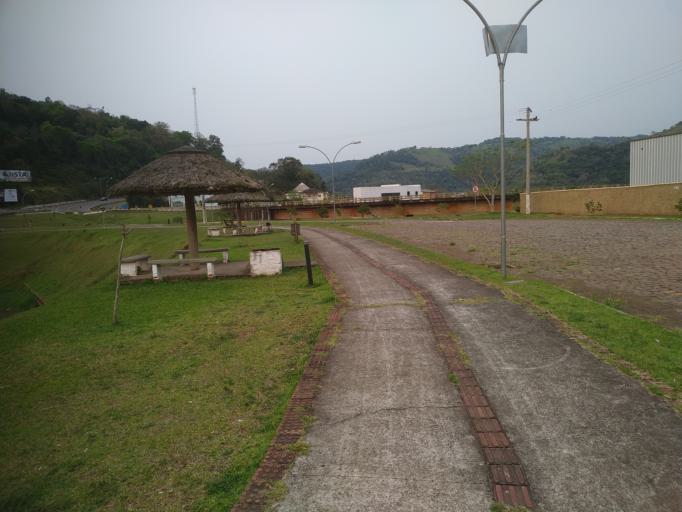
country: BR
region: Santa Catarina
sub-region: Chapeco
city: Chapeco
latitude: -27.2820
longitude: -52.6936
